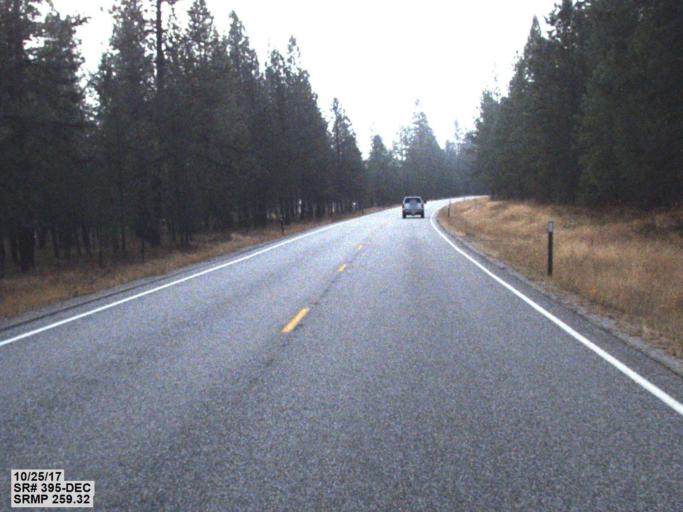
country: US
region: Washington
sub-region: Stevens County
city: Kettle Falls
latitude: 48.8532
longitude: -118.2021
